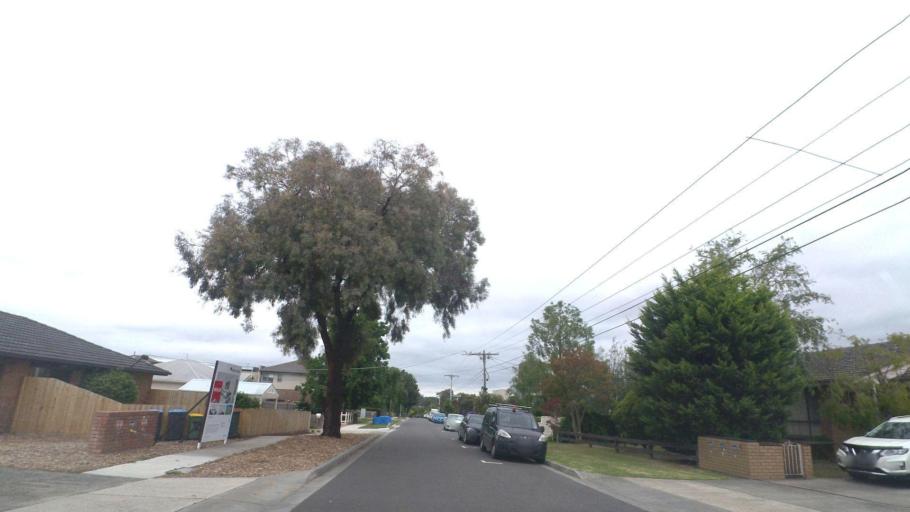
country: AU
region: Victoria
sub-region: Knox
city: Boronia
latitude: -37.8627
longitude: 145.2792
